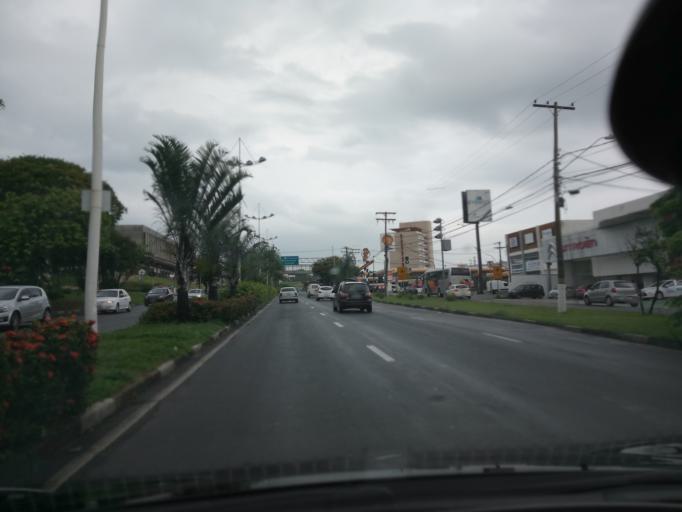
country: BR
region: Sao Paulo
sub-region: Campinas
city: Campinas
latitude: -22.9285
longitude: -47.0692
